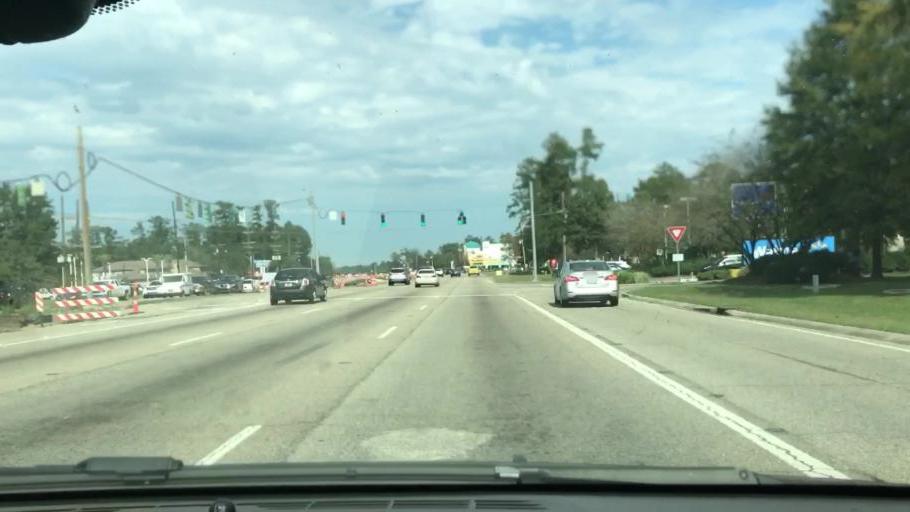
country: US
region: Louisiana
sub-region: Saint Tammany Parish
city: Covington
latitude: 30.4434
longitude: -90.0823
